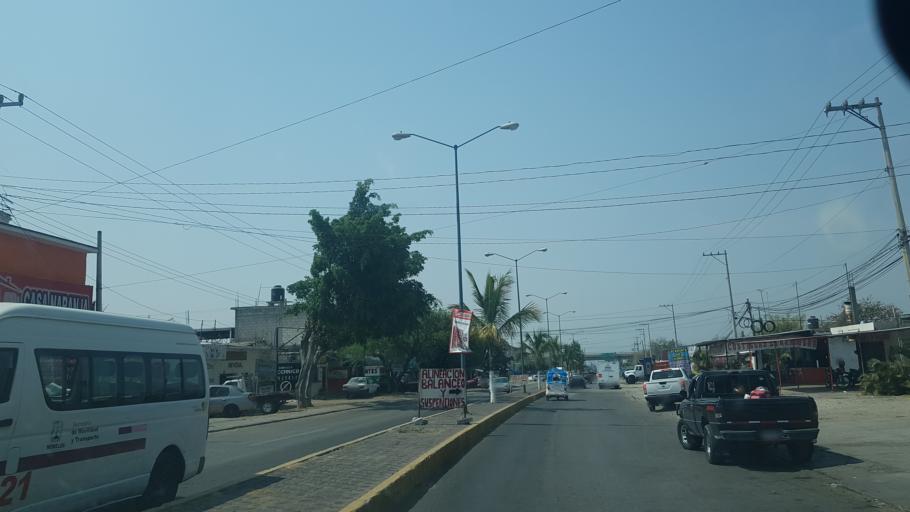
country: MX
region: Morelos
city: Amayuca
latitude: 18.7202
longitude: -98.7941
